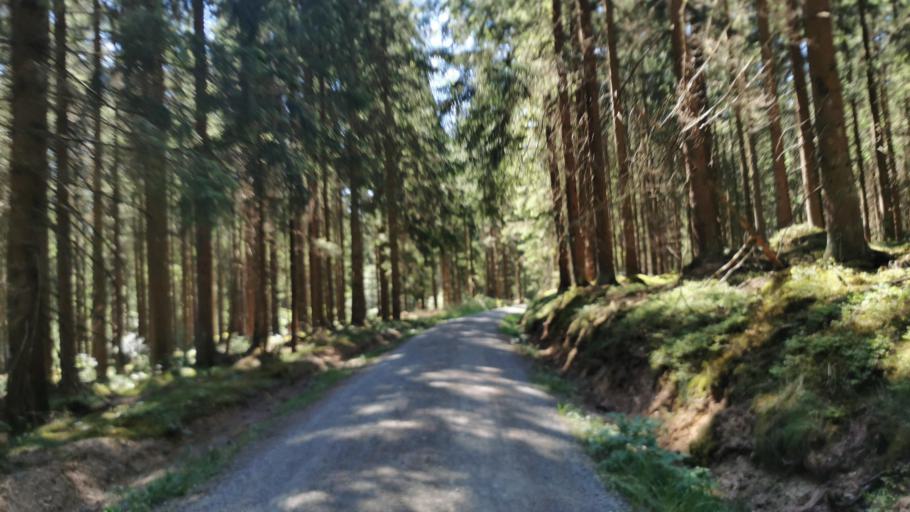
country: DE
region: Bavaria
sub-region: Upper Franconia
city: Pressig
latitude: 50.4086
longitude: 11.2908
